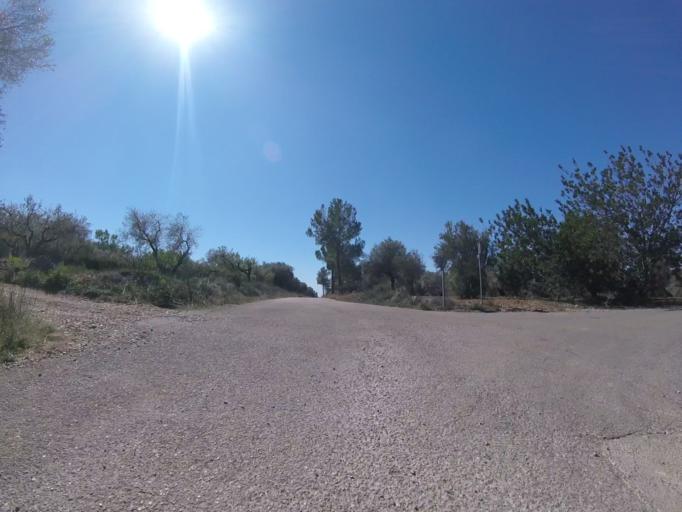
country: ES
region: Valencia
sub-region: Provincia de Castello
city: Cuevas de Vinroma
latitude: 40.3908
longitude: 0.1609
